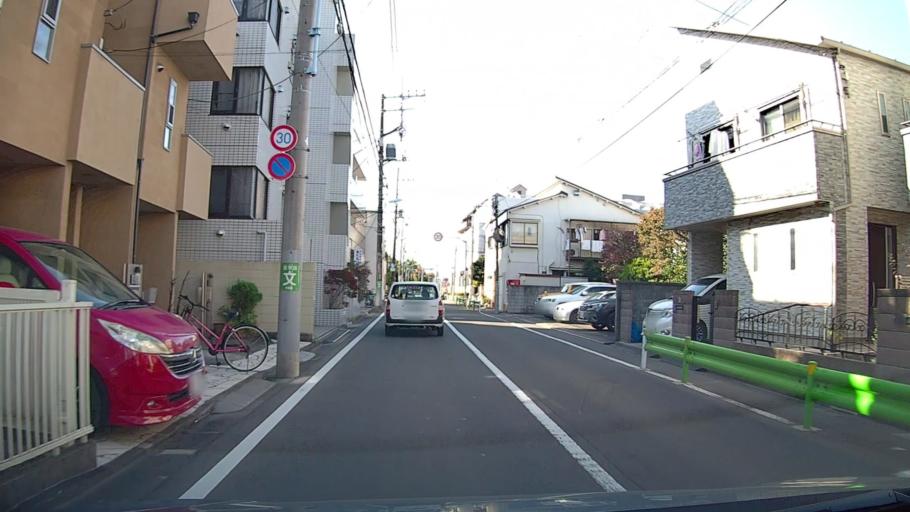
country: JP
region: Tokyo
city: Musashino
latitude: 35.7148
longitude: 139.6097
